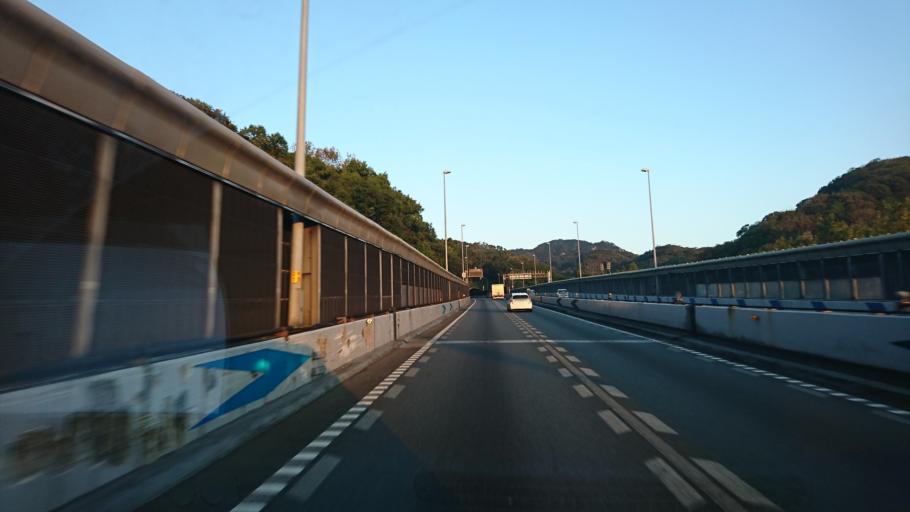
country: JP
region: Hyogo
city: Kobe
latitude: 34.6534
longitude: 135.1192
